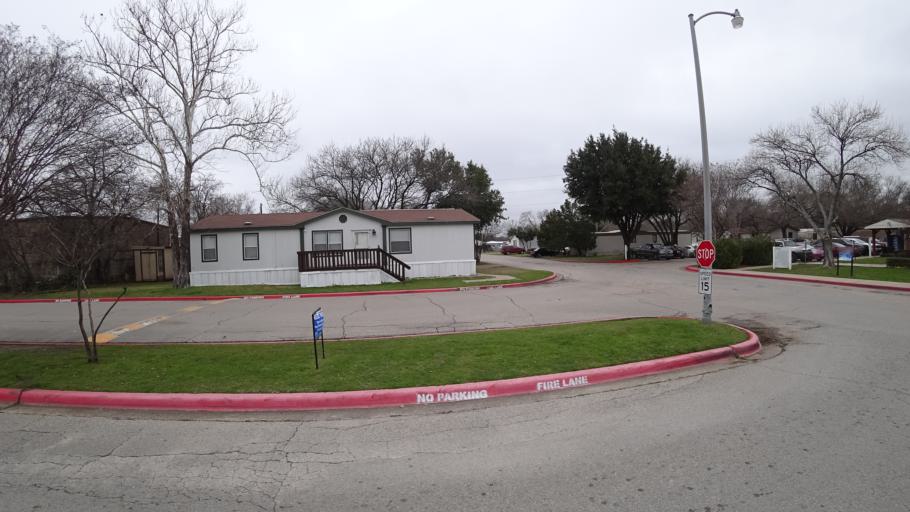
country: US
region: Texas
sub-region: Denton County
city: Lewisville
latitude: 33.0603
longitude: -97.0001
